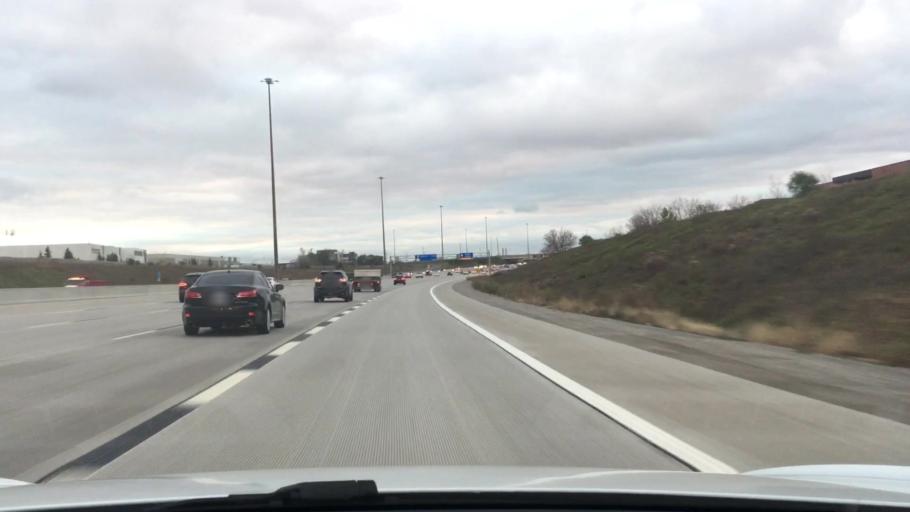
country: CA
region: Ontario
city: Concord
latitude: 43.7964
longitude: -79.4882
